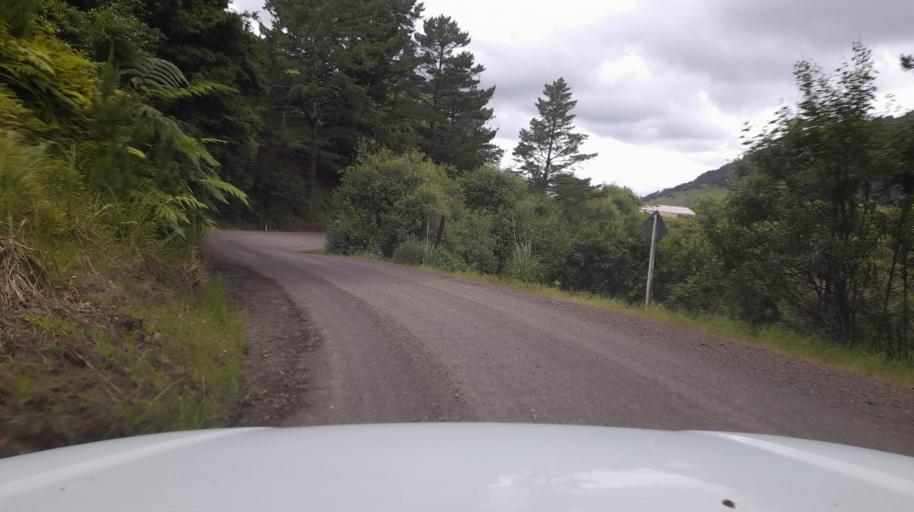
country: NZ
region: Northland
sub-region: Far North District
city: Kaitaia
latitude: -35.3291
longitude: 173.3539
